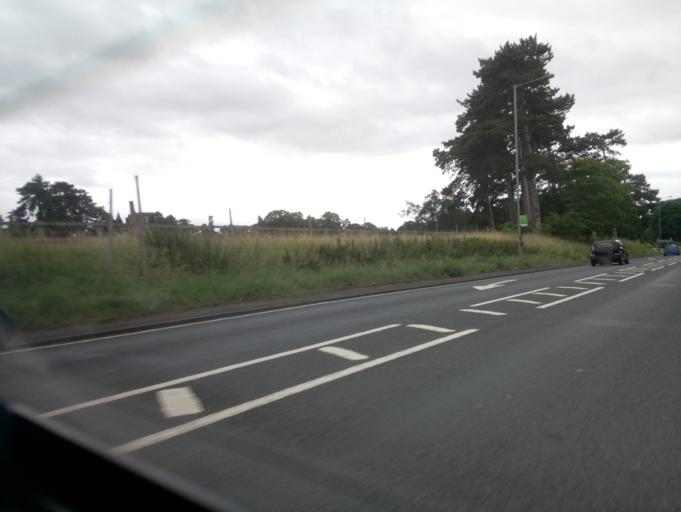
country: GB
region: England
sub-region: Worcestershire
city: Droitwich
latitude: 52.2772
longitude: -2.1351
